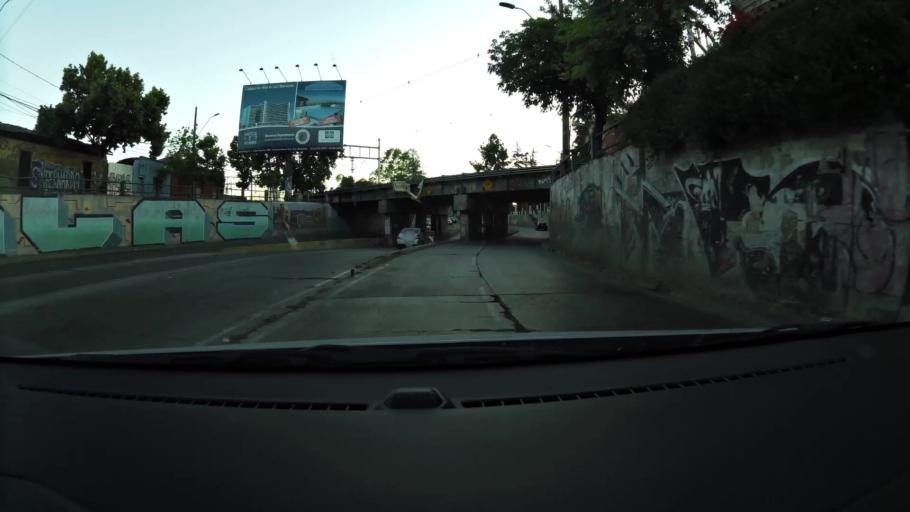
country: CL
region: Santiago Metropolitan
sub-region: Provincia de Maipo
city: San Bernardo
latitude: -33.5847
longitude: -70.6984
